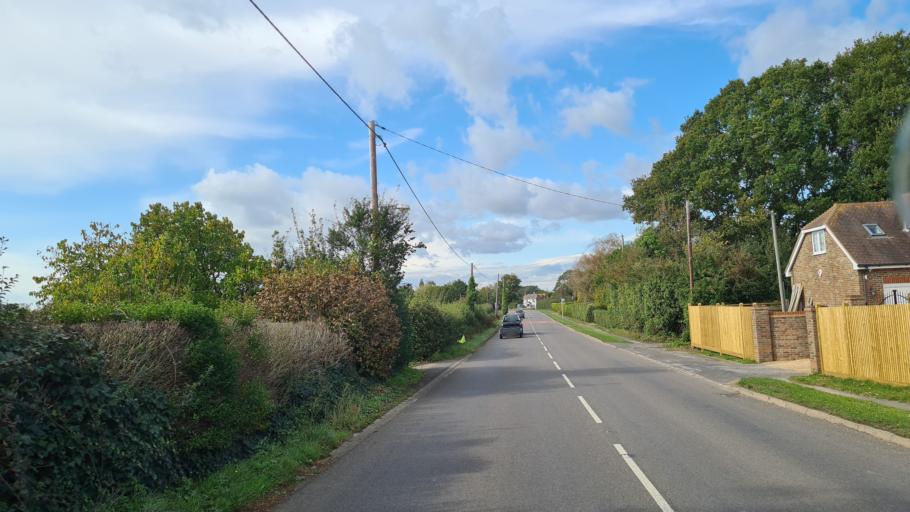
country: GB
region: England
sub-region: East Sussex
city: Hailsham
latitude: 50.8793
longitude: 0.2782
